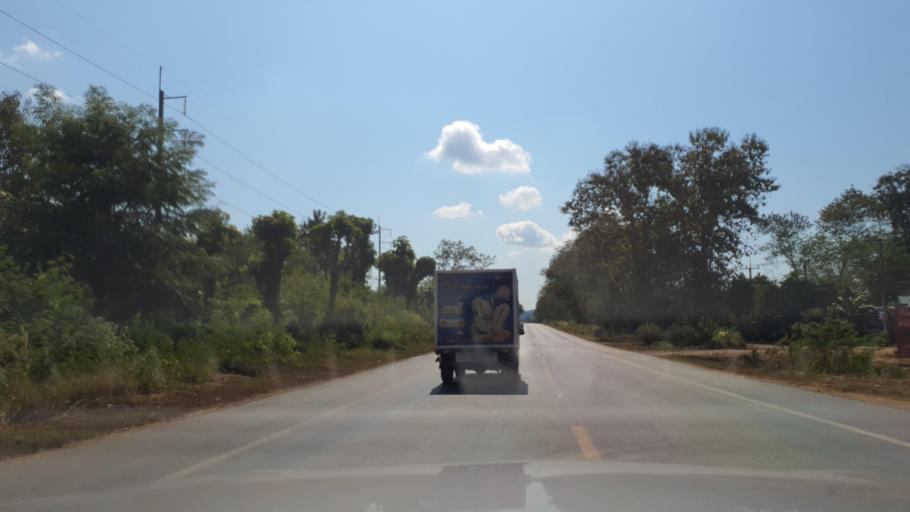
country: TH
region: Nan
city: Tha Wang Pha
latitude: 19.0558
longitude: 100.8069
